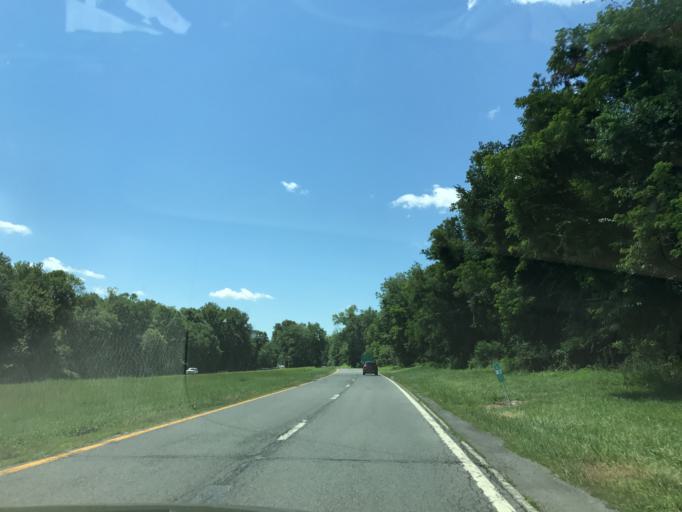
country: US
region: New York
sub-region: Dutchess County
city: Hillside Lake
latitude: 41.6047
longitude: -73.7633
